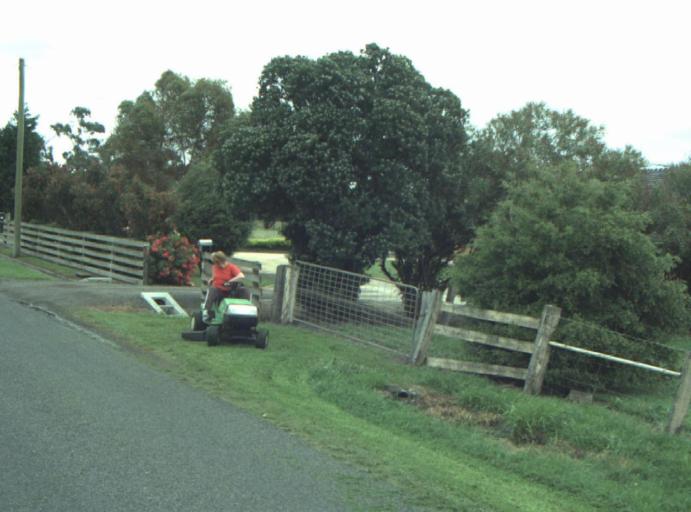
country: AU
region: Victoria
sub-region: Greater Geelong
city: Bell Post Hill
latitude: -38.0538
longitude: 144.3171
